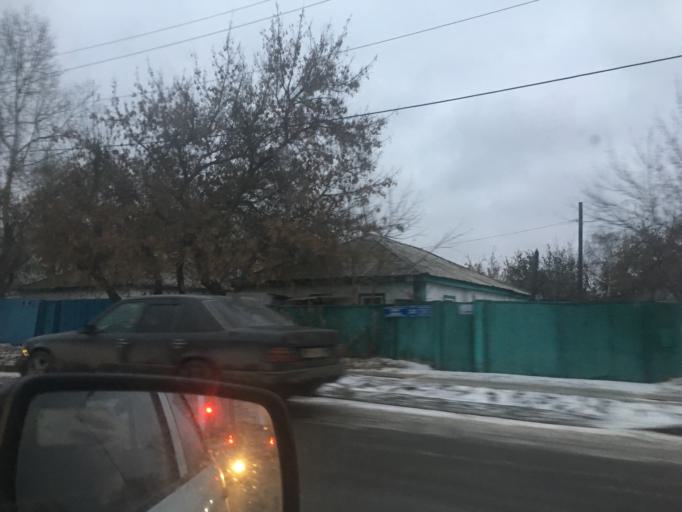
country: KZ
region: Astana Qalasy
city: Astana
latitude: 51.1653
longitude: 71.4468
